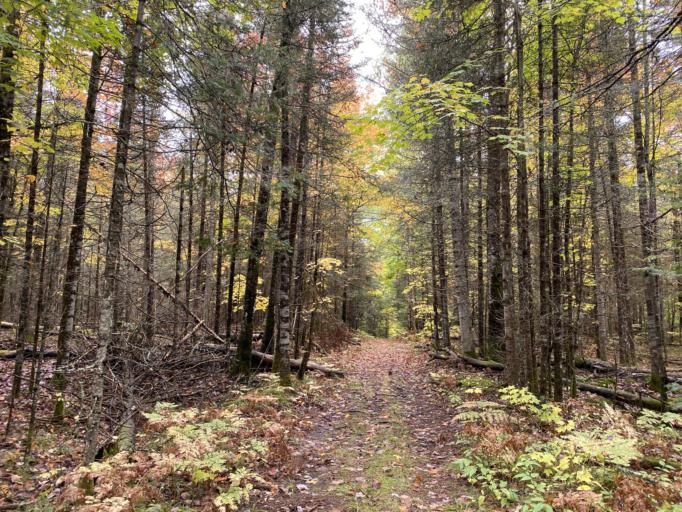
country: US
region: Michigan
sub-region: Marquette County
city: West Ishpeming
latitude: 46.5325
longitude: -87.9982
